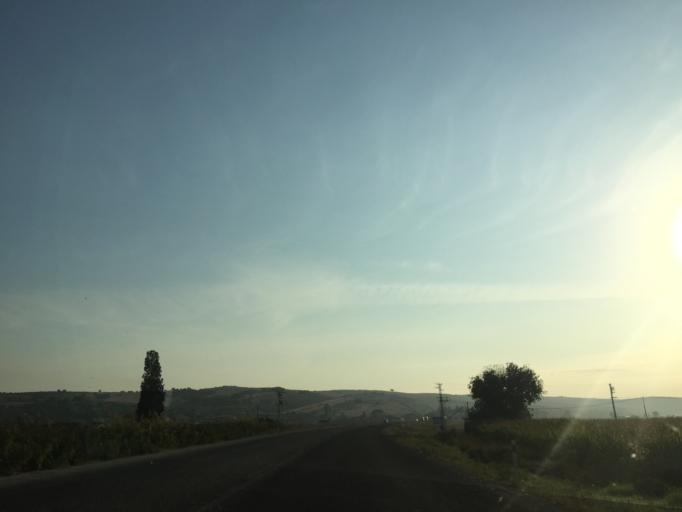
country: TR
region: Balikesir
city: Aksakal
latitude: 40.0897
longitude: 28.0572
